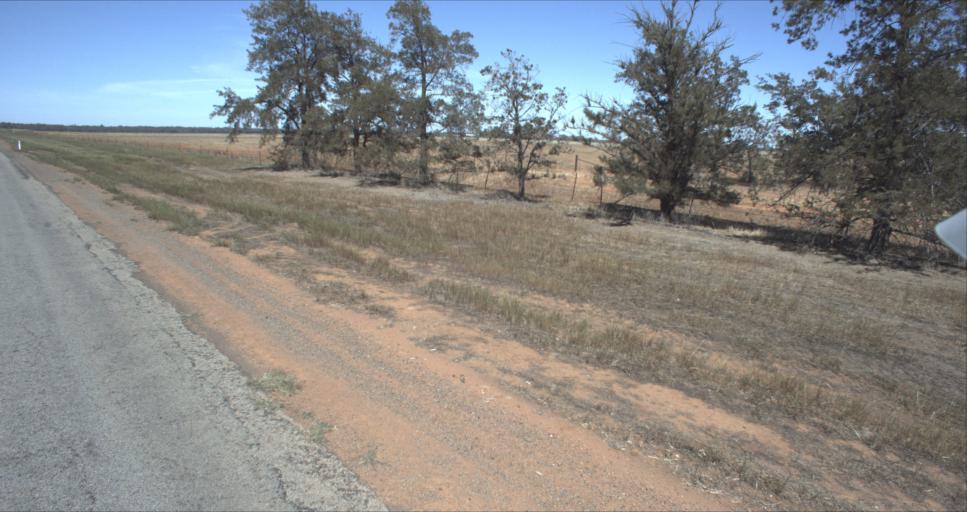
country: AU
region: New South Wales
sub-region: Leeton
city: Leeton
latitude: -34.5779
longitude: 146.3094
